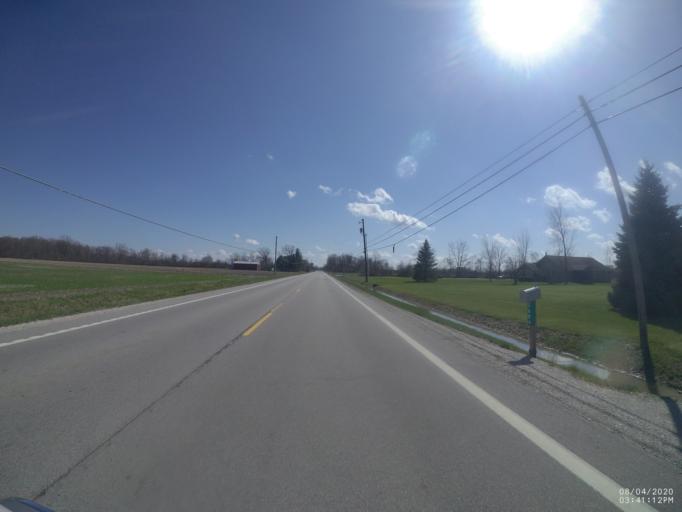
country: US
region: Ohio
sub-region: Sandusky County
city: Stony Prairie
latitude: 41.2644
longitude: -83.2353
